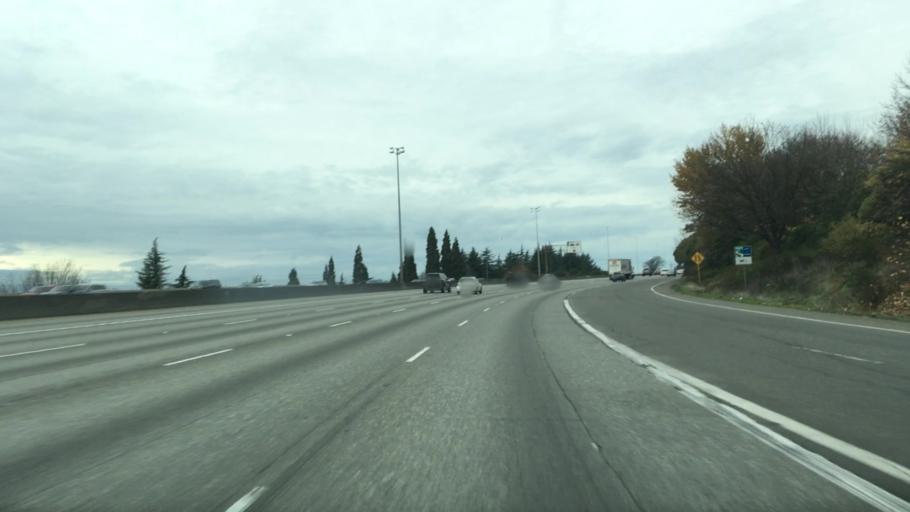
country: US
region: Washington
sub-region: King County
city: White Center
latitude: 47.5515
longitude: -122.3163
